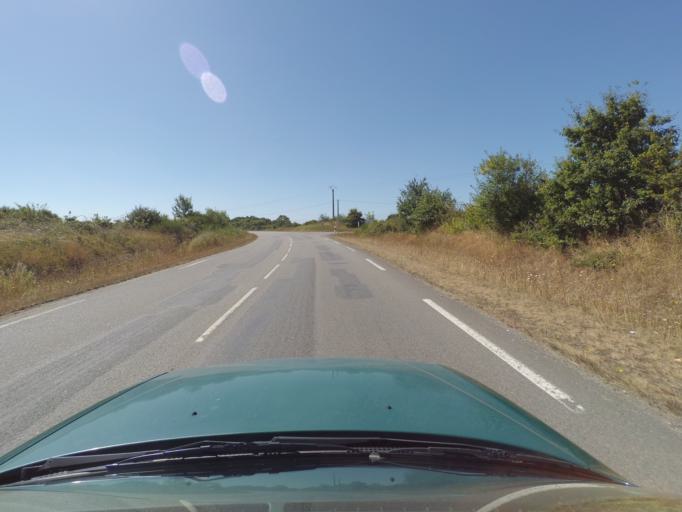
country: FR
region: Pays de la Loire
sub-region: Departement de la Loire-Atlantique
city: Les Sorinieres
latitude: 47.1311
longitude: -1.5158
